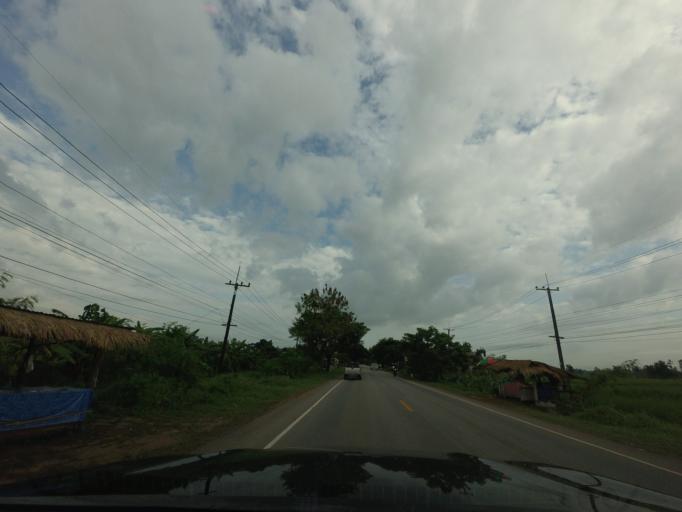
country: TH
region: Changwat Udon Thani
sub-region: Amphoe Ban Phue
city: Ban Phue
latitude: 17.7512
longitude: 102.3988
